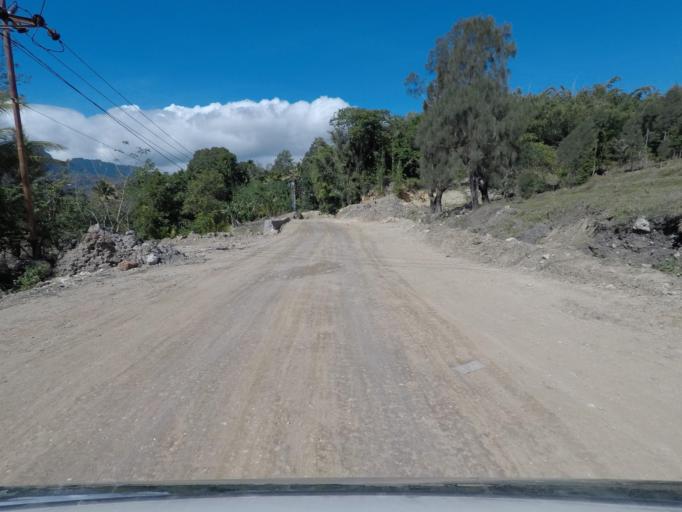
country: TL
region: Baucau
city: Venilale
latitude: -8.6552
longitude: 126.3701
